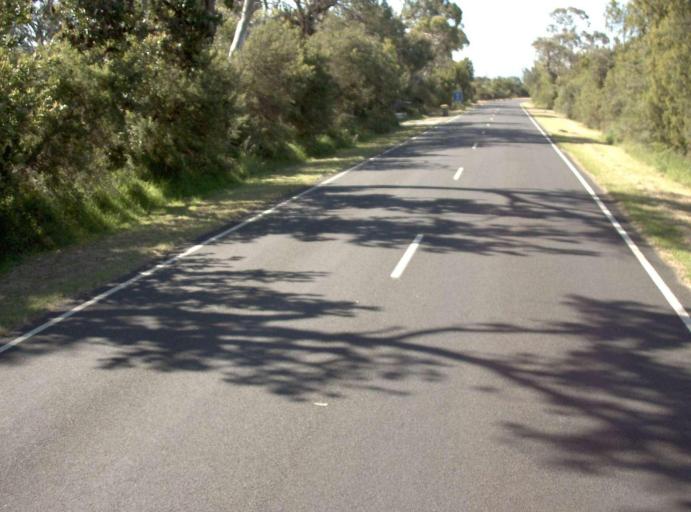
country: AU
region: Victoria
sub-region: Latrobe
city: Traralgon
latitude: -38.6455
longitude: 146.6723
